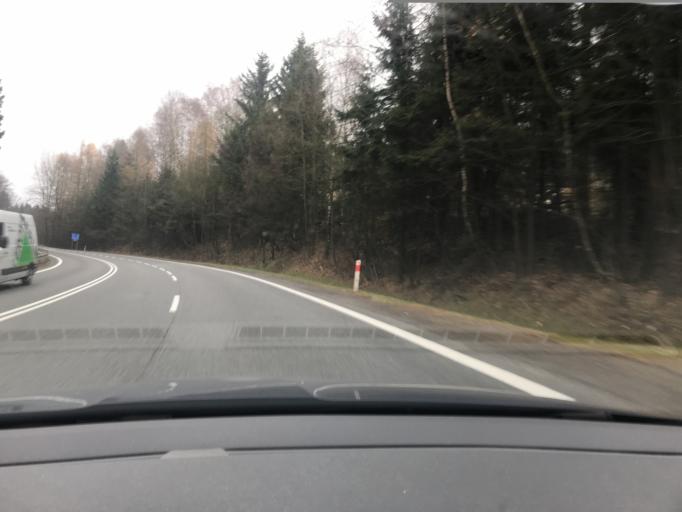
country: PL
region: Lower Silesian Voivodeship
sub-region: Powiat klodzki
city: Duszniki-Zdroj
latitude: 50.3993
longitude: 16.3427
